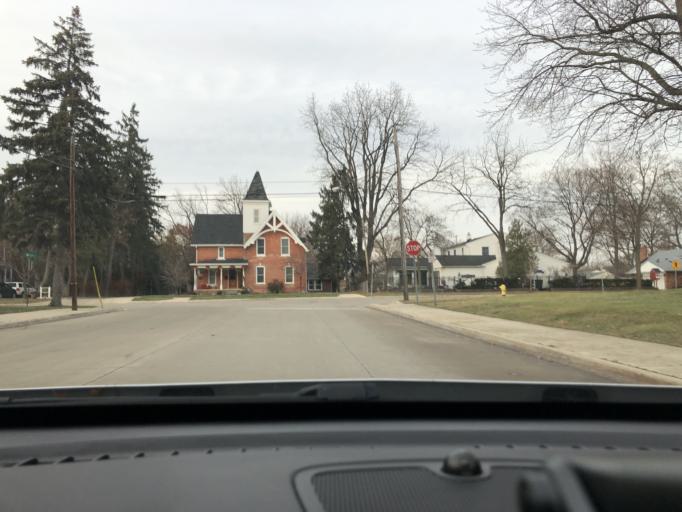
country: US
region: Michigan
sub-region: Wayne County
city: Dearborn Heights
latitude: 42.3076
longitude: -83.2468
